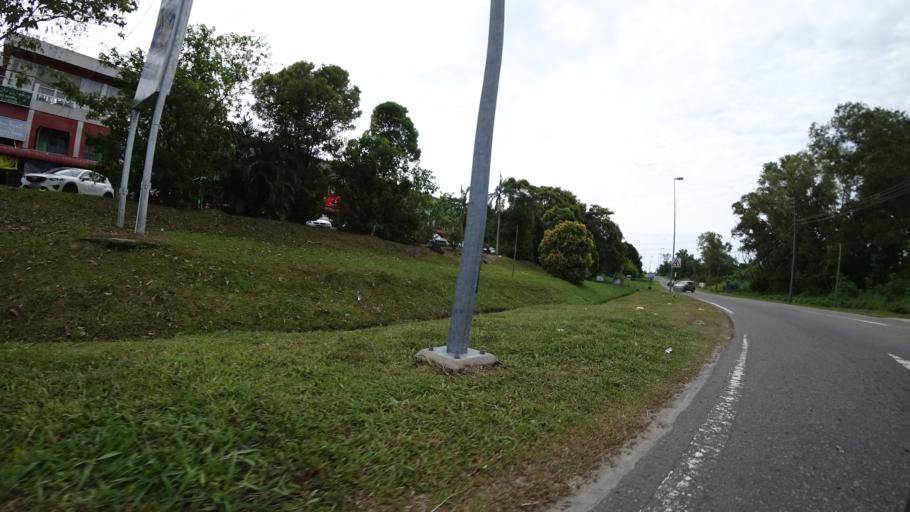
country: BN
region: Brunei and Muara
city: Bandar Seri Begawan
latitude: 4.9298
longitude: 114.8852
